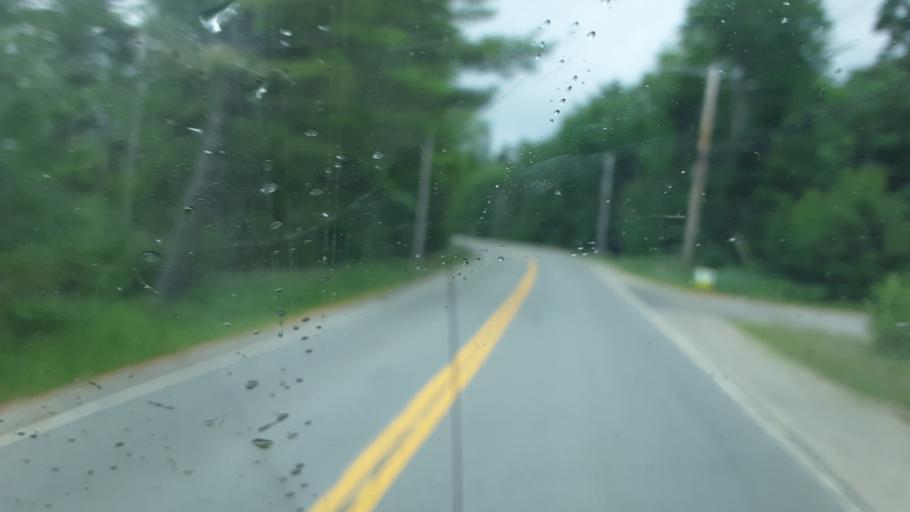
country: US
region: Maine
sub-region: Penobscot County
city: Millinocket
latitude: 45.6855
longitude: -68.7742
